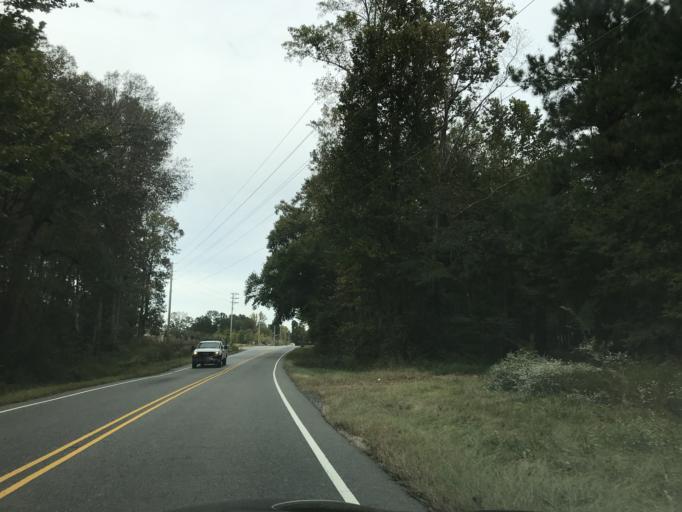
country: US
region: North Carolina
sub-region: Wake County
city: Rolesville
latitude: 35.9007
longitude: -78.5069
